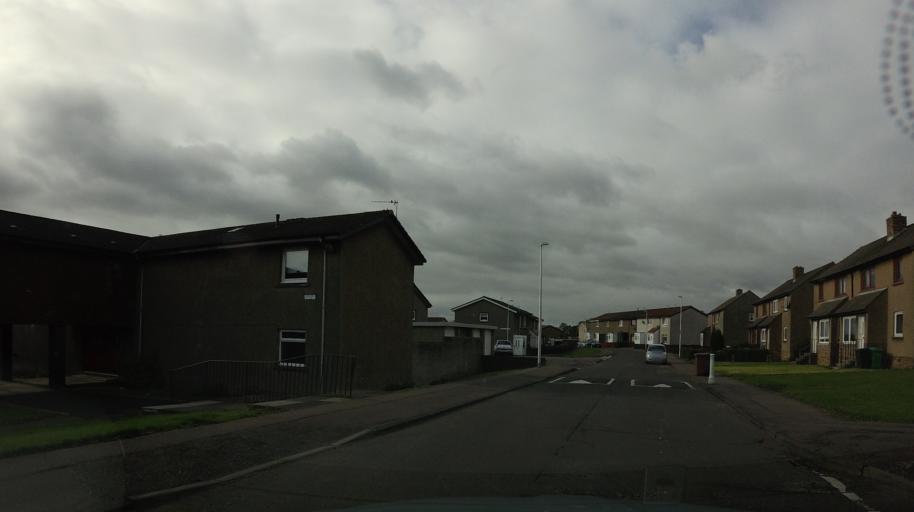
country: GB
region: Scotland
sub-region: Fife
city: Cowdenbeath
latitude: 56.1054
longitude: -3.3451
